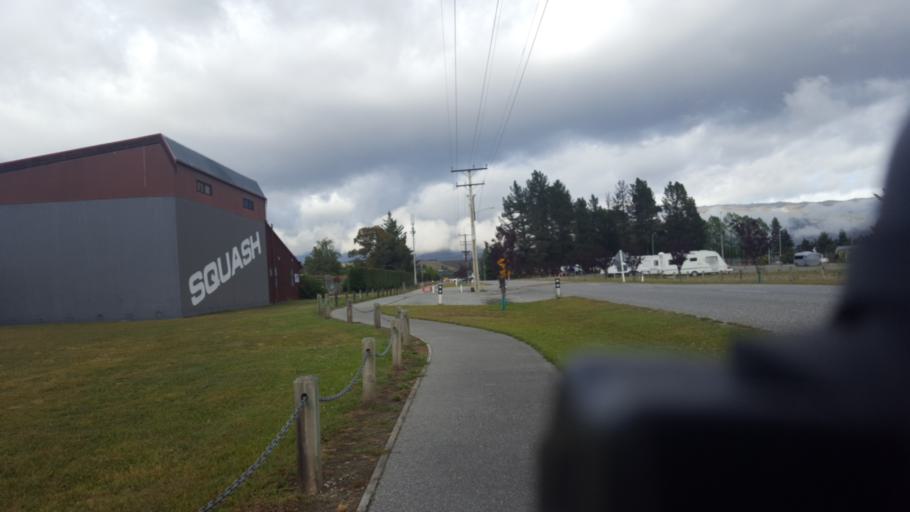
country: NZ
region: Otago
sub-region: Queenstown-Lakes District
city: Wanaka
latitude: -45.2430
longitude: 169.3817
